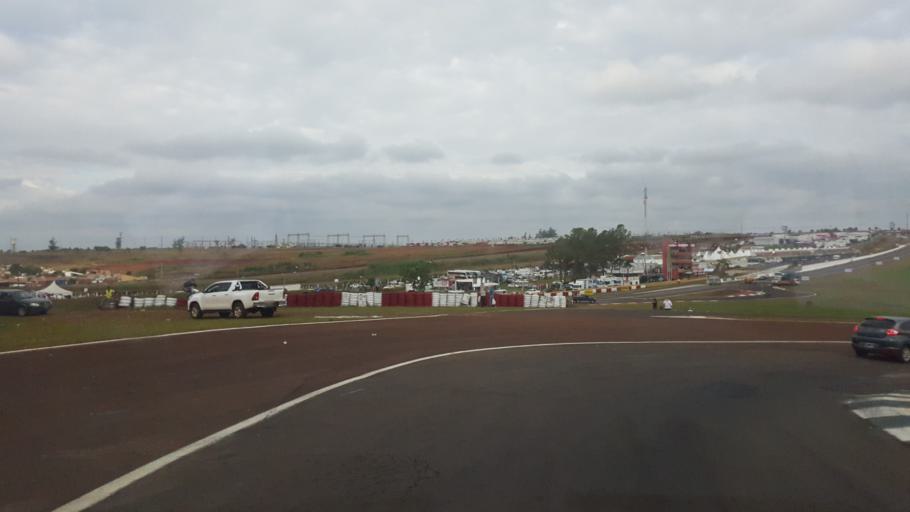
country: AR
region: Misiones
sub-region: Departamento de Capital
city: Posadas
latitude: -27.4358
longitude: -55.9273
